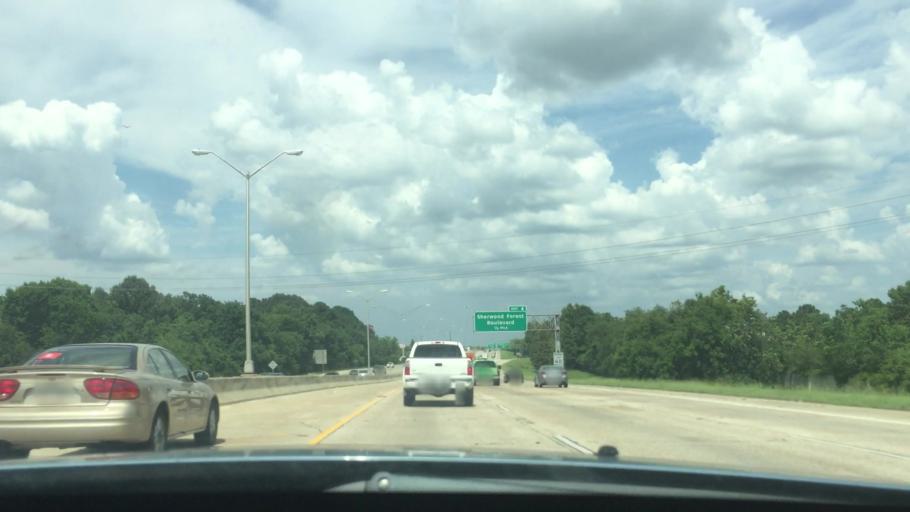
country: US
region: Louisiana
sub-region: East Baton Rouge Parish
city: Westminster
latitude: 30.4283
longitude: -91.0656
